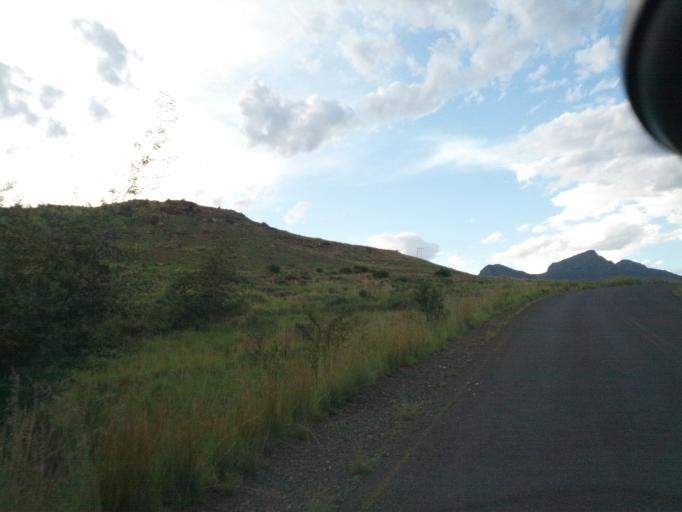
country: LS
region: Qacha's Nek
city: Qacha's Nek
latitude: -30.0677
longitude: 28.6171
